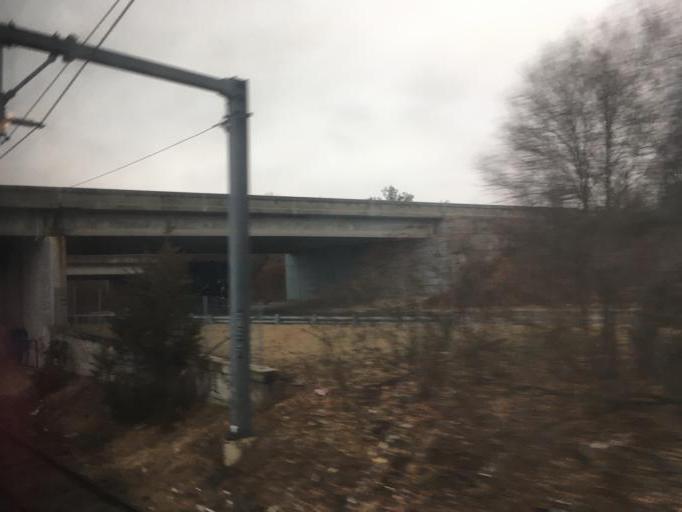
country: US
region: Massachusetts
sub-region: Bristol County
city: Mansfield Center
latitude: 42.0138
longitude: -71.2334
